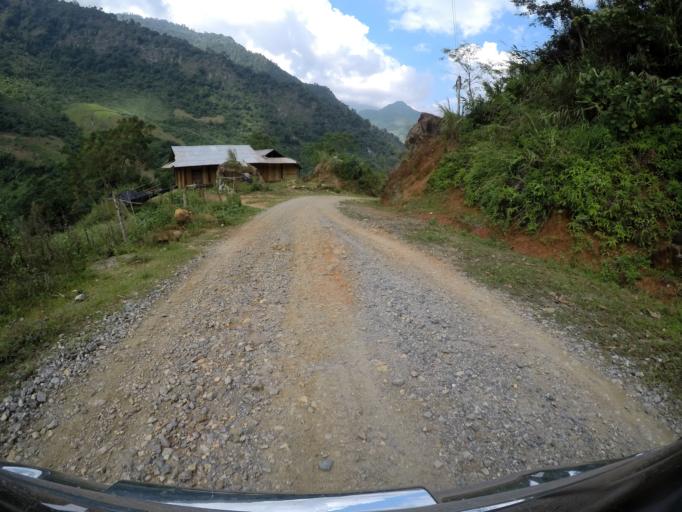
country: VN
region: Yen Bai
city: Son Thinh
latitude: 21.6820
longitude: 104.5618
